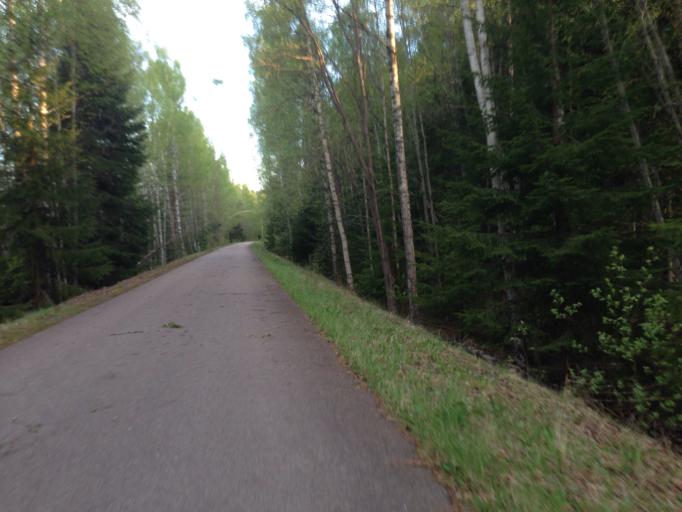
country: SE
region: Dalarna
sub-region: Ludvika Kommun
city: Grangesberg
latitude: 60.1282
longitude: 15.0702
